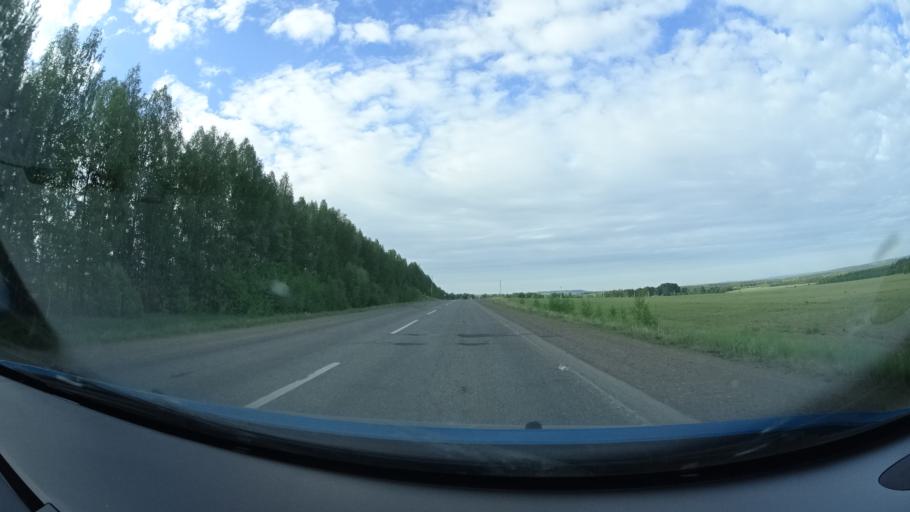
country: RU
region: Perm
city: Osa
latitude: 57.3812
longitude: 55.6091
